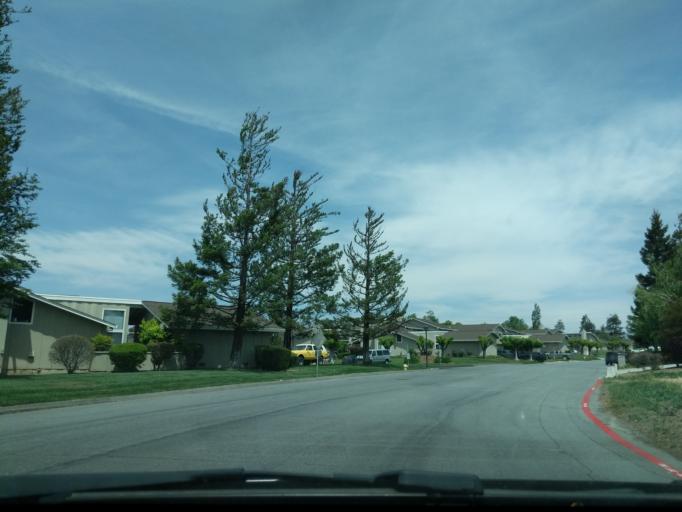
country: US
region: California
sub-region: San Benito County
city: Ridgemark
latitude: 36.8106
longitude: -121.3635
